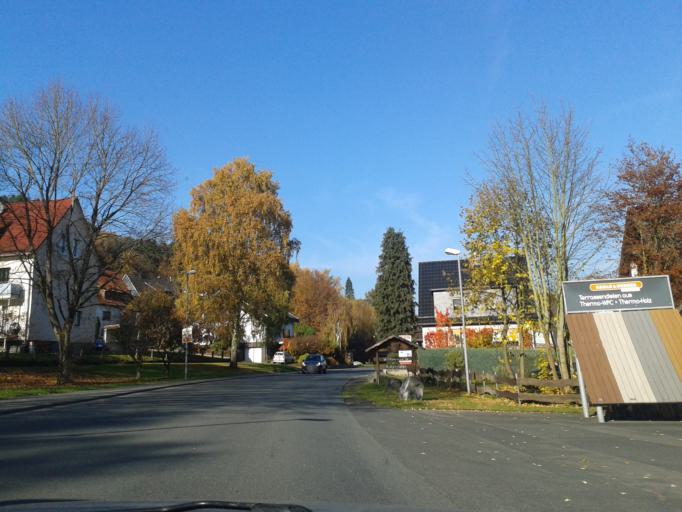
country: DE
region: Hesse
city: Dillenburg
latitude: 50.8243
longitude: 8.3338
